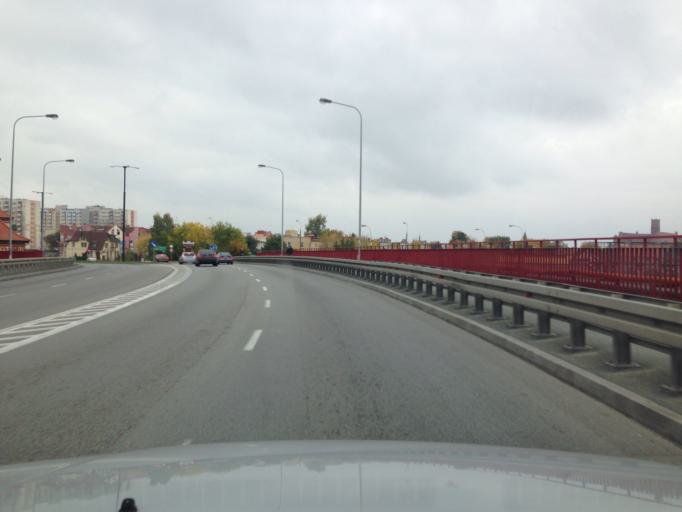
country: PL
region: Pomeranian Voivodeship
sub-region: Powiat malborski
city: Malbork
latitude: 54.0376
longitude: 19.0404
